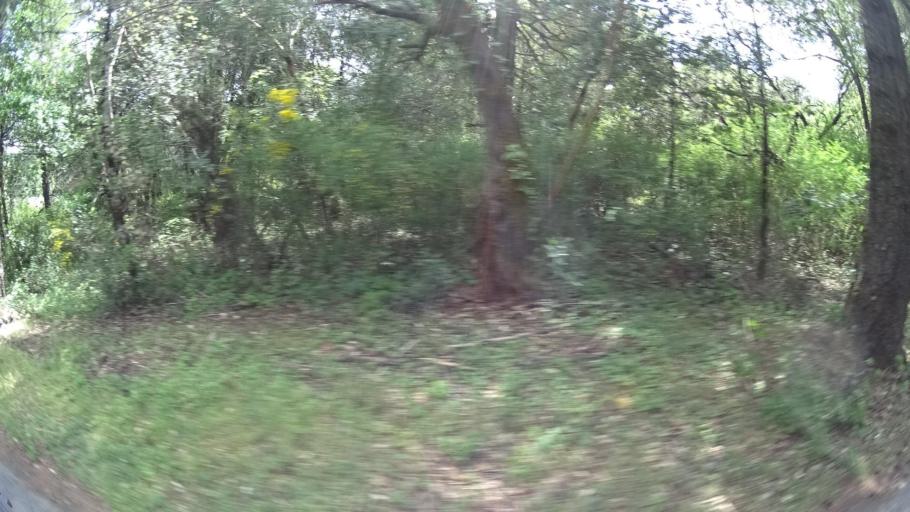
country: US
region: California
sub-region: Humboldt County
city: Redway
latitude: 40.0918
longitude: -123.8052
